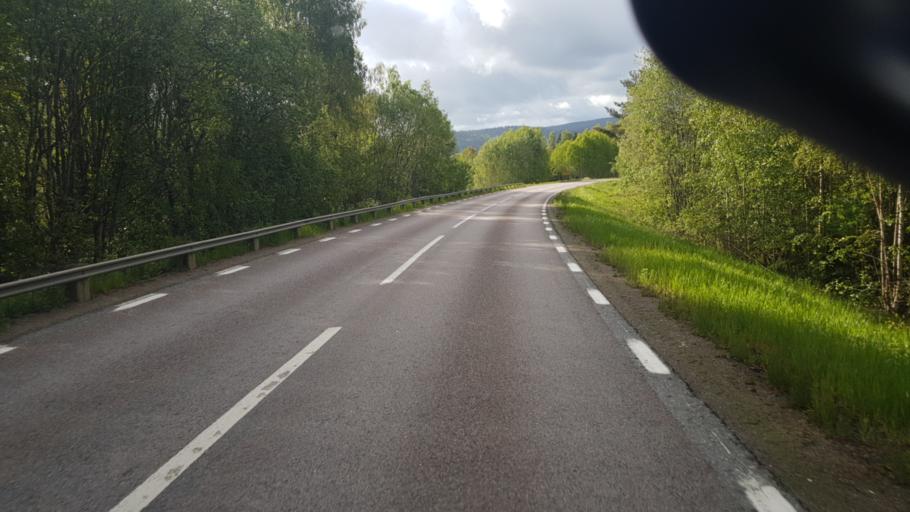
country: SE
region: Vaermland
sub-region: Eda Kommun
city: Amotfors
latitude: 59.7254
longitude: 12.2792
